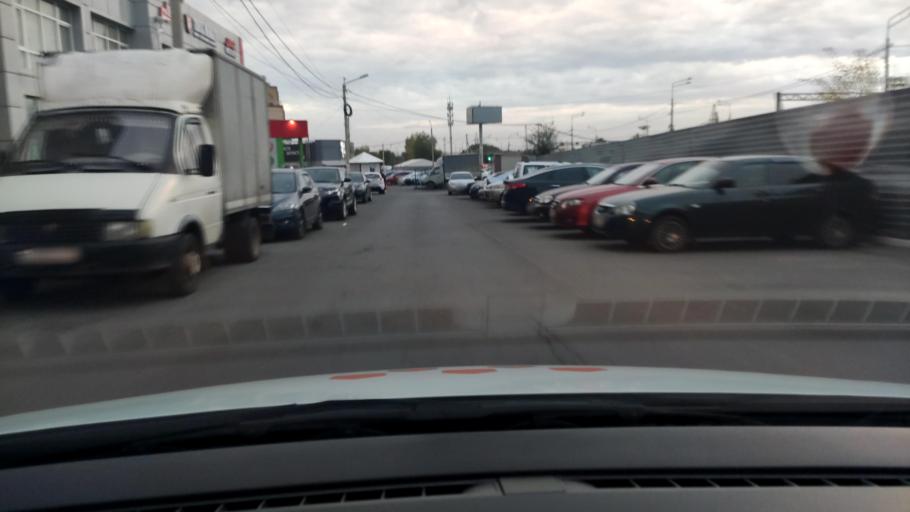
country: RU
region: Voronezj
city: Podgornoye
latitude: 51.7151
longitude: 39.1445
